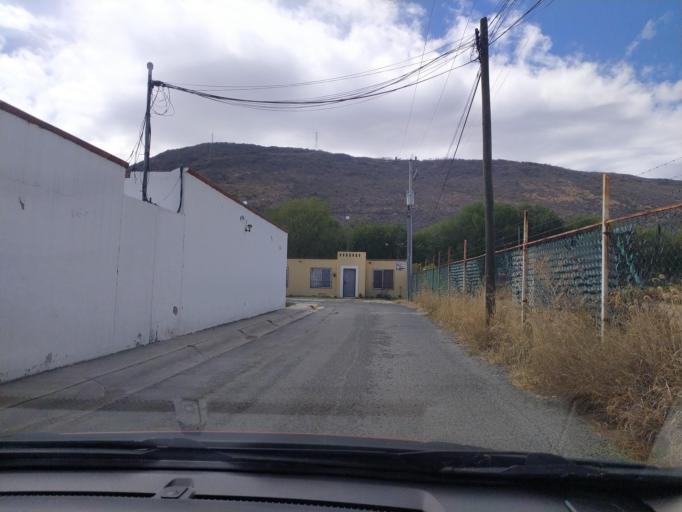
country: MX
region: Guanajuato
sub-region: Purisima del Rincon
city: Monte Grande
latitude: 21.0177
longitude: -101.8907
